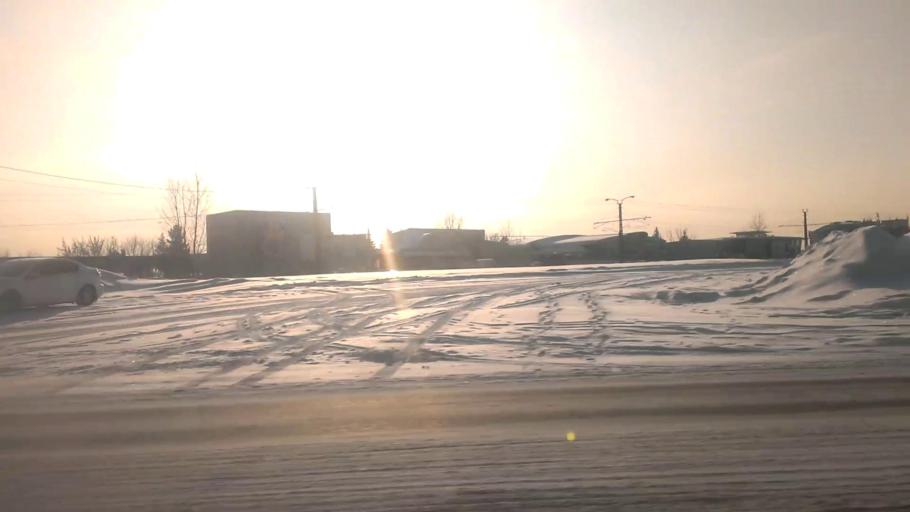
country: RU
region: Altai Krai
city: Novosilikatnyy
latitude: 53.3303
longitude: 83.6625
